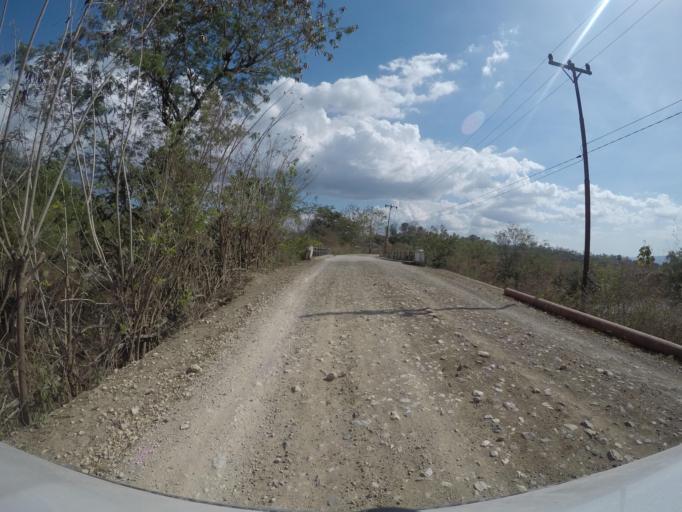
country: TL
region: Bobonaro
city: Maliana
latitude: -8.9973
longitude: 125.1984
